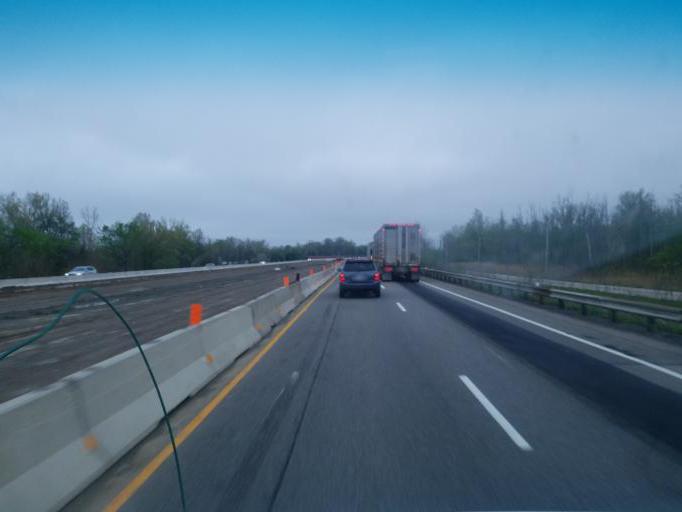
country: US
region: Ohio
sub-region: Summit County
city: Northfield
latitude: 41.3478
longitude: -81.5114
